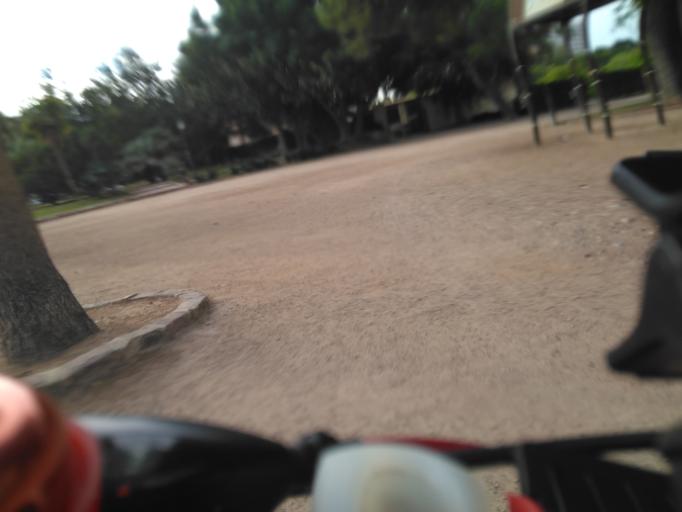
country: ES
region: Valencia
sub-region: Provincia de Valencia
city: Valencia
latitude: 39.4813
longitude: -0.3675
